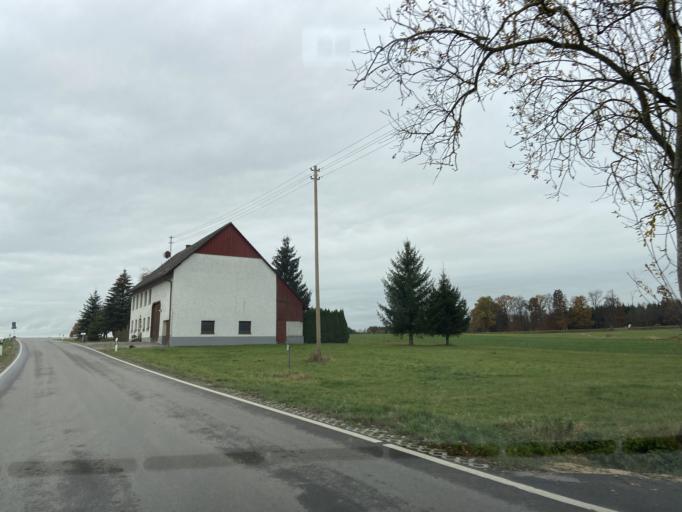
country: DE
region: Baden-Wuerttemberg
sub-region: Tuebingen Region
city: Wald
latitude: 47.9710
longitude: 9.1563
